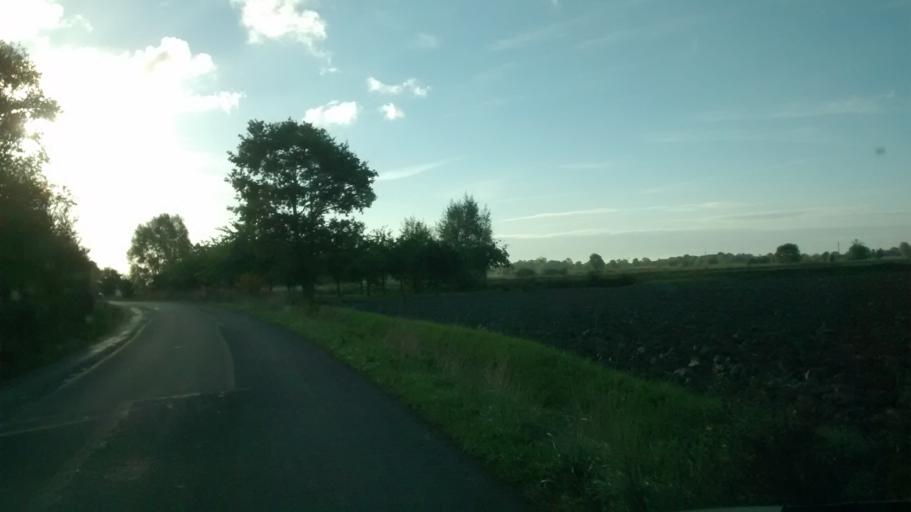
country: FR
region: Brittany
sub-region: Departement d'Ille-et-Vilaine
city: La Gouesniere
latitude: 48.6269
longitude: -1.8719
